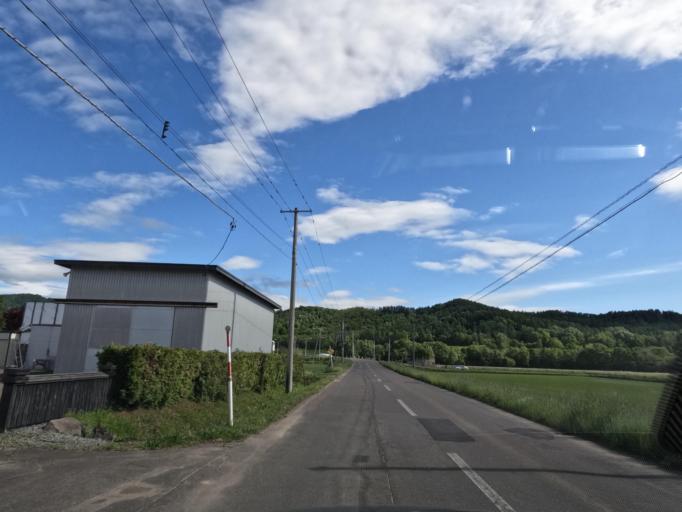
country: JP
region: Hokkaido
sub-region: Asahikawa-shi
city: Asahikawa
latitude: 43.7531
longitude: 142.5252
